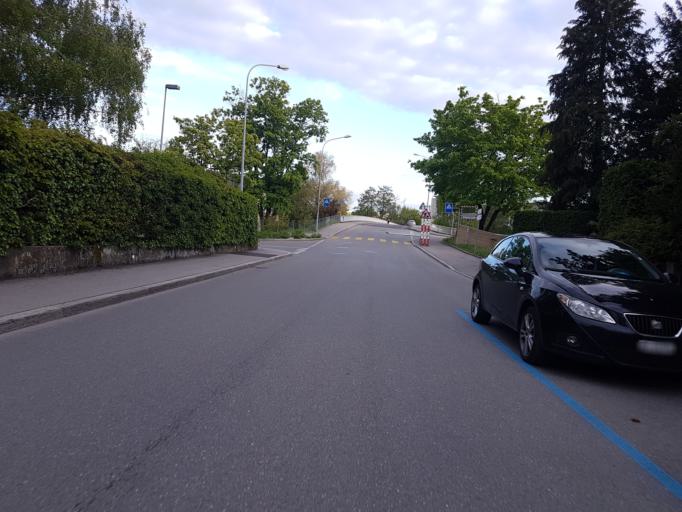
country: CH
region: Bern
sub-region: Biel/Bienne District
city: Nidau
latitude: 47.1237
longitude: 7.2371
